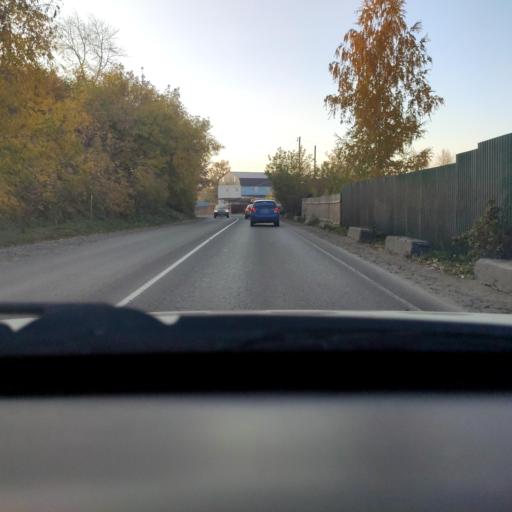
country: RU
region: Perm
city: Kondratovo
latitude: 57.9645
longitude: 56.1281
